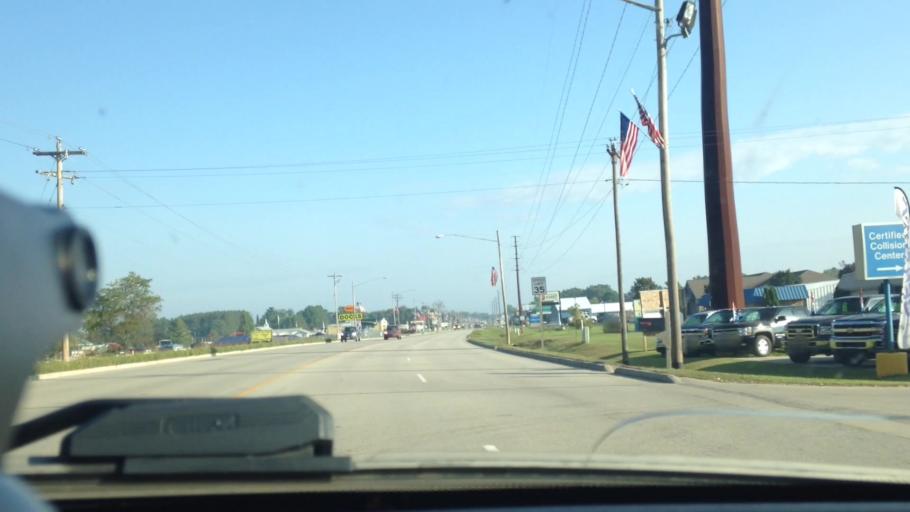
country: US
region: Wisconsin
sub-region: Marinette County
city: Peshtigo
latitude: 45.2194
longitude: -87.9970
